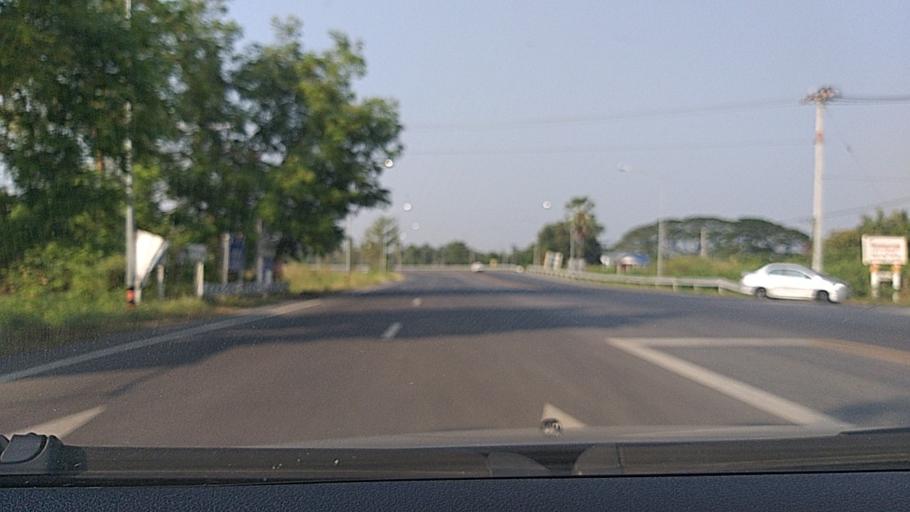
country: TH
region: Sing Buri
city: Phrom Buri
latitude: 14.7929
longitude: 100.4440
